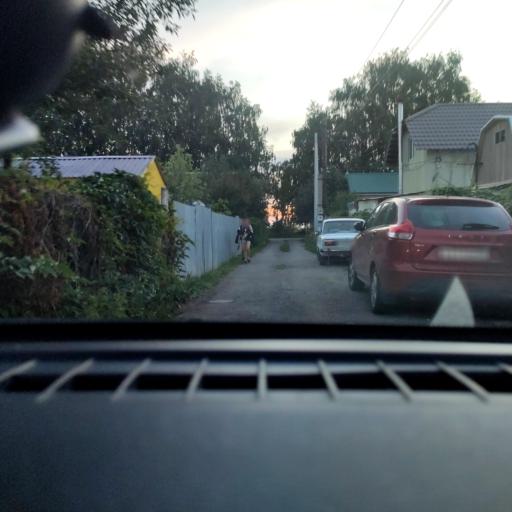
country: RU
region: Samara
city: Tol'yatti
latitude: 53.6324
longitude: 49.4043
